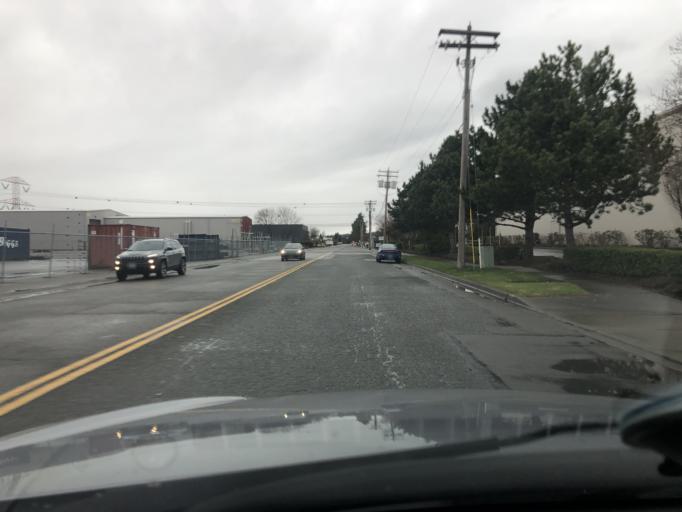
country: US
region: Washington
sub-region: King County
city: Auburn
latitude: 47.3345
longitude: -122.2265
